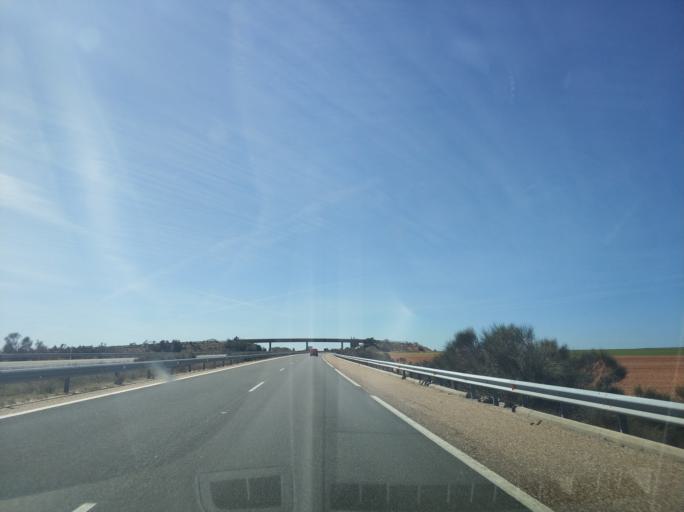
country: ES
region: Castille and Leon
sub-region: Provincia de Salamanca
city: Parada de Rubiales
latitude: 41.1533
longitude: -5.4570
